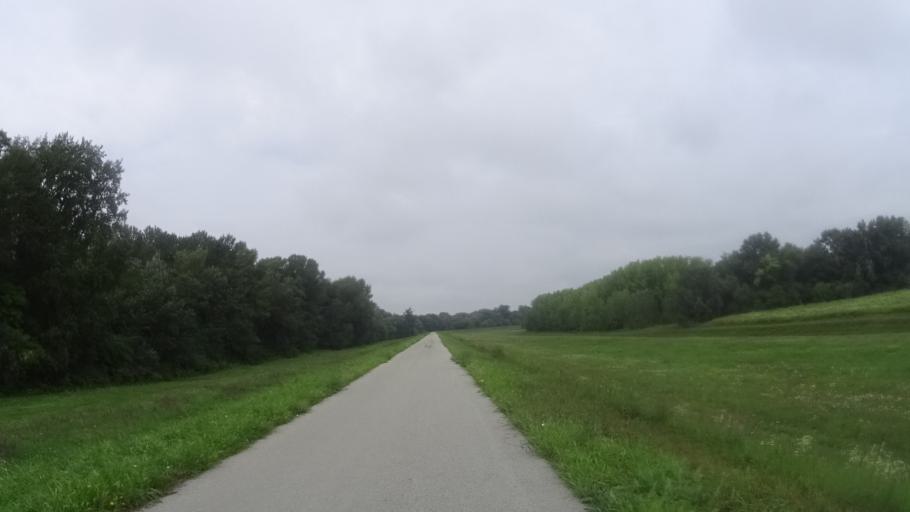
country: SK
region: Nitriansky
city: Komarno
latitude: 47.7512
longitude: 18.1524
